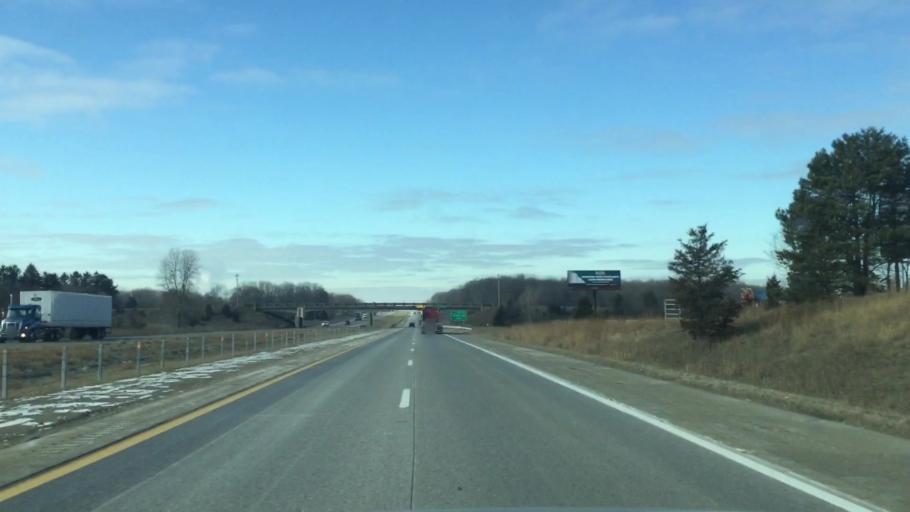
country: US
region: Michigan
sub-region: Calhoun County
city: Albion
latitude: 42.2651
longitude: -84.7336
